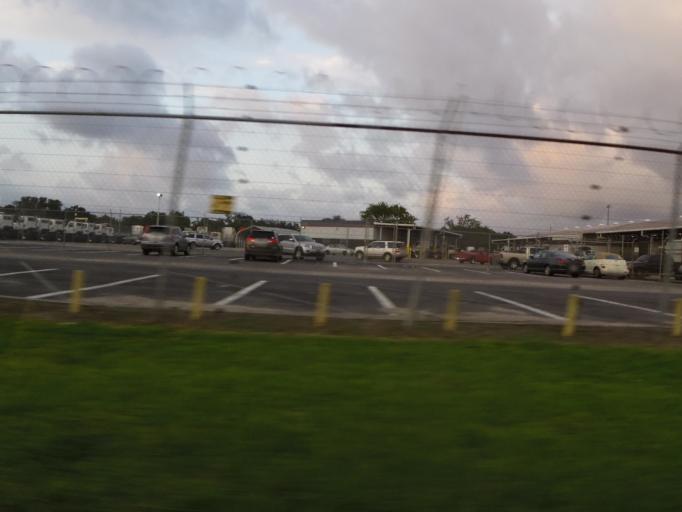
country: US
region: Florida
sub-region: Duval County
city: Jacksonville
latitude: 30.3202
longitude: -81.7264
